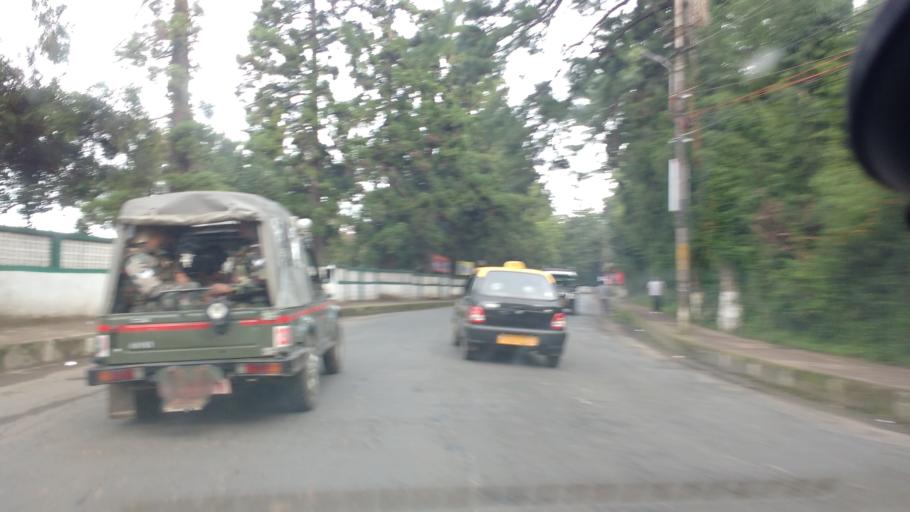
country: IN
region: Meghalaya
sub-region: East Khasi Hills
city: Shillong
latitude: 25.5686
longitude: 91.8801
